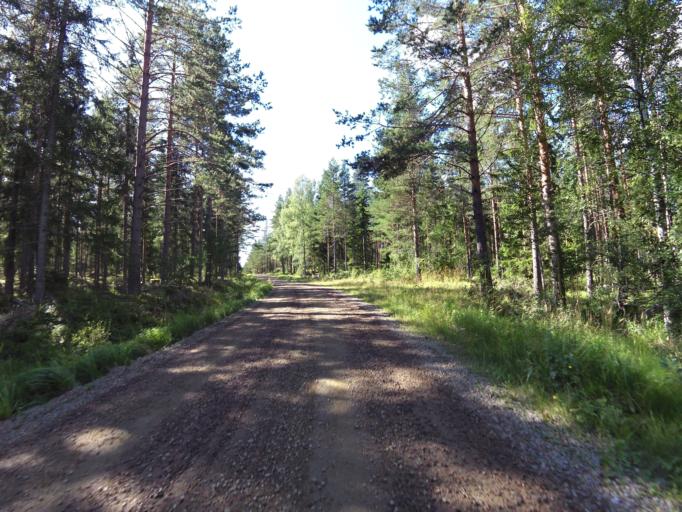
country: SE
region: Gaevleborg
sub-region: Ockelbo Kommun
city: Ockelbo
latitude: 60.7964
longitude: 16.8279
